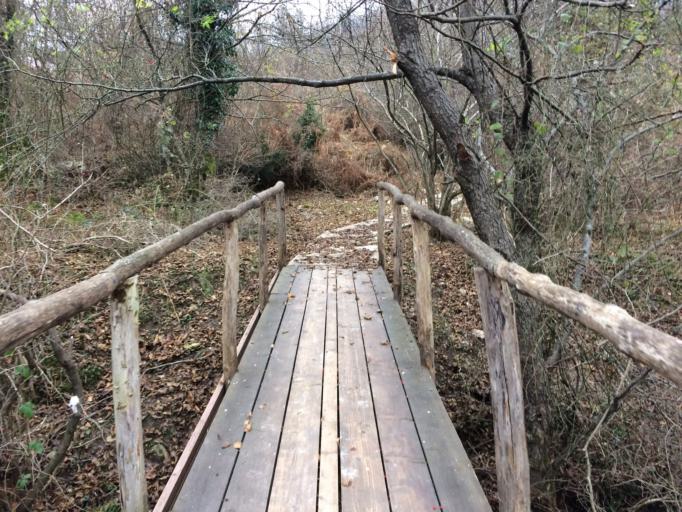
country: GE
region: Imereti
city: Tsqaltubo
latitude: 42.4552
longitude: 42.5467
